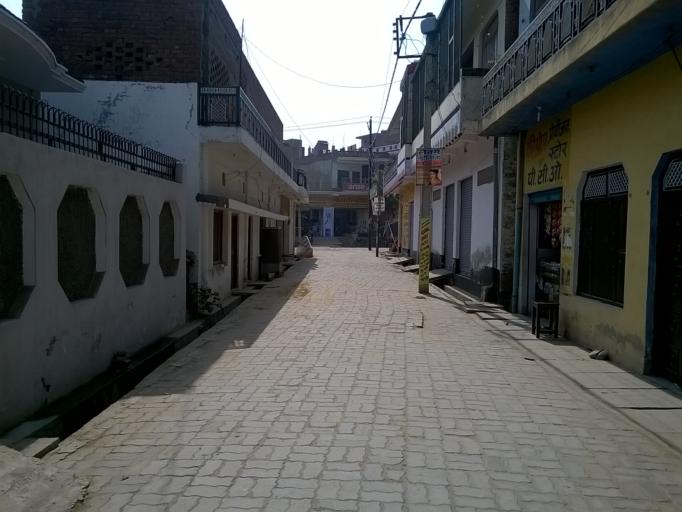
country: IN
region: Uttar Pradesh
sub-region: Etawah
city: Etawah
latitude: 26.7892
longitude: 79.0395
